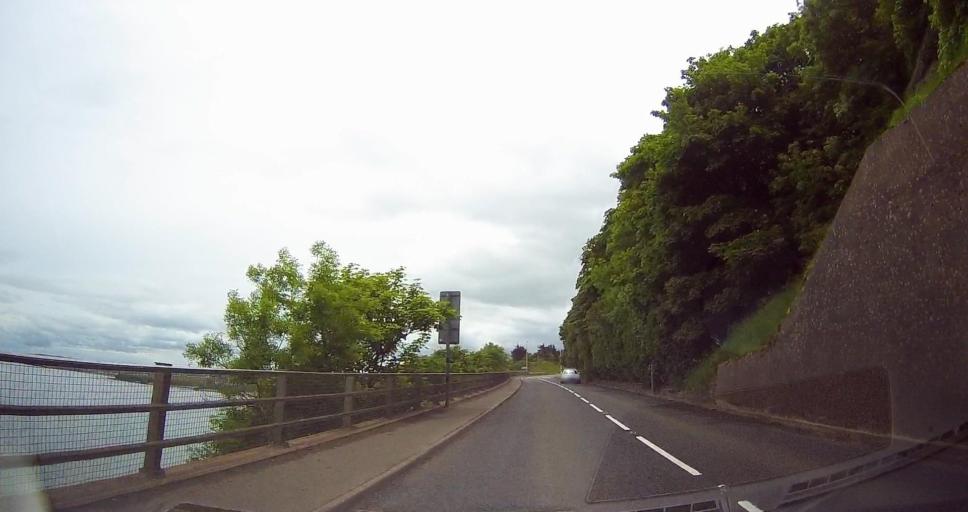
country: GB
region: Scotland
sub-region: Highland
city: Thurso
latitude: 58.6078
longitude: -3.5518
